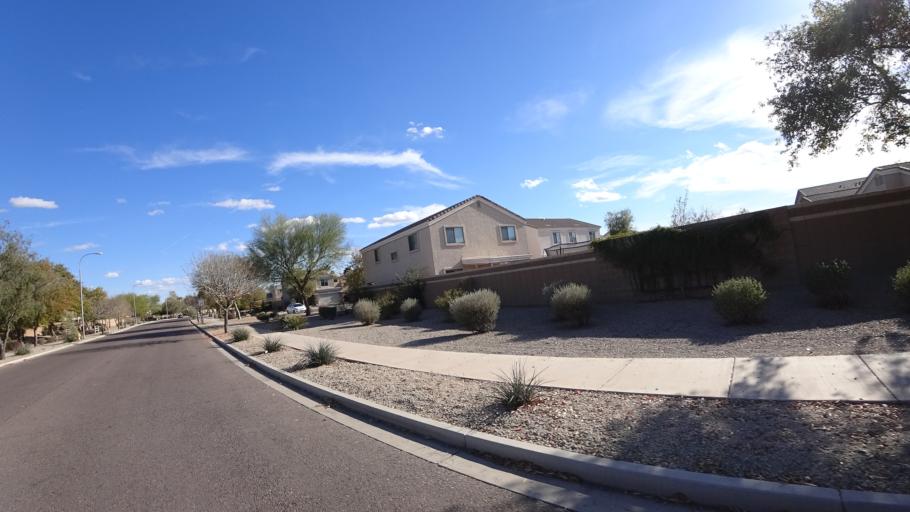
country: US
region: Arizona
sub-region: Maricopa County
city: Tolleson
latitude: 33.4196
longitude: -112.2448
